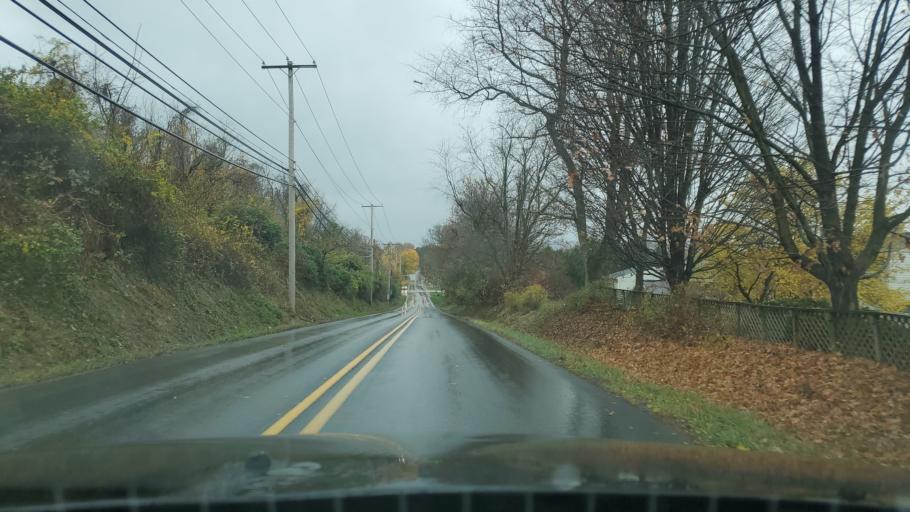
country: US
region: Pennsylvania
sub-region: Cumberland County
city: Mechanicsburg
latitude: 40.1645
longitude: -77.0020
